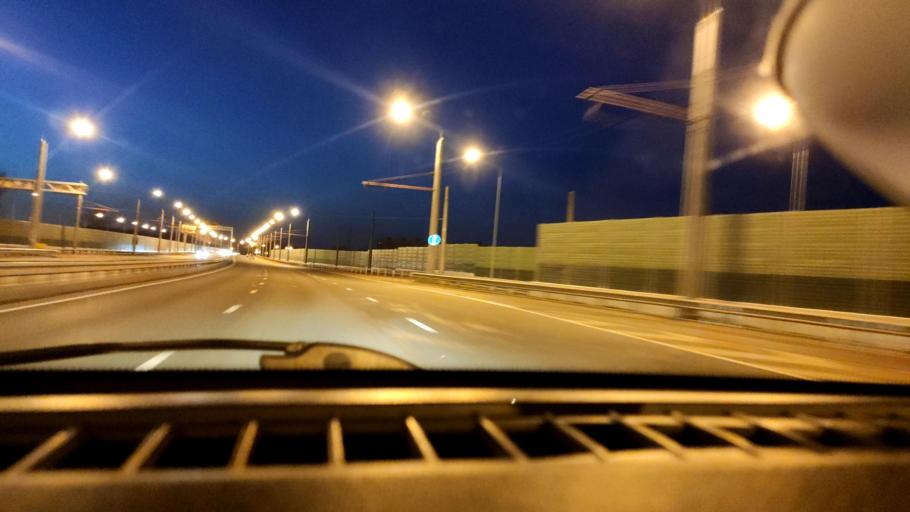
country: RU
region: Samara
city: Samara
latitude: 53.1640
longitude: 50.0863
